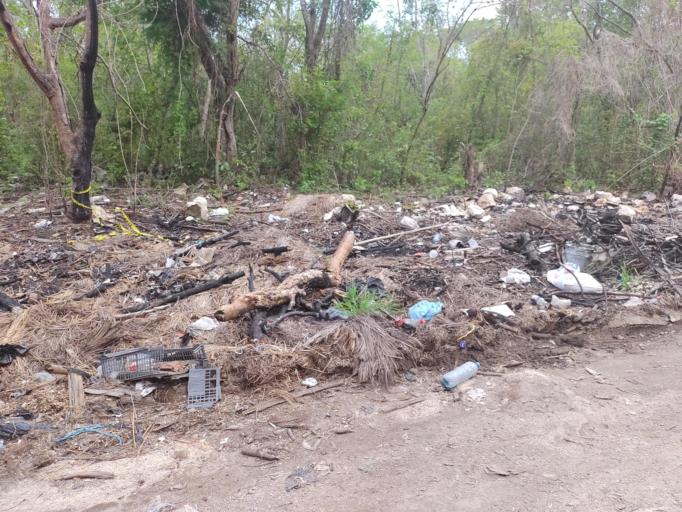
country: MX
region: Quintana Roo
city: Tulum
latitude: 20.2057
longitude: -87.4708
